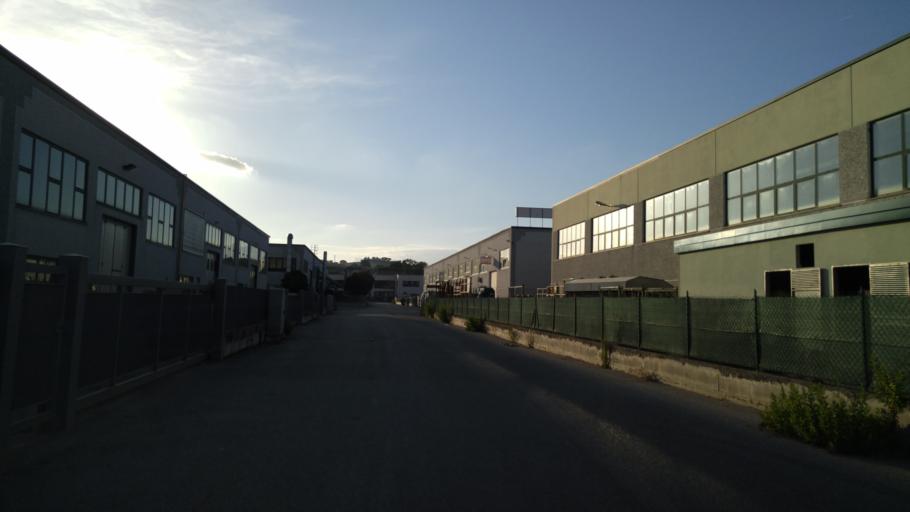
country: IT
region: The Marches
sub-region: Provincia di Pesaro e Urbino
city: Lucrezia
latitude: 43.7617
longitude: 12.9336
